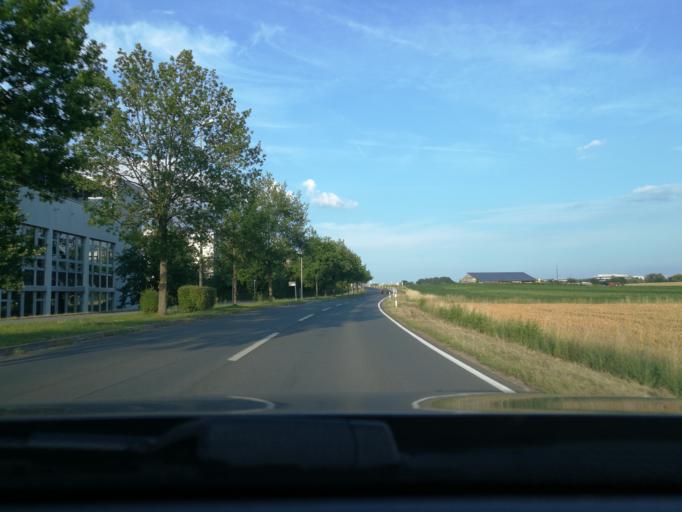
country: DE
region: Bavaria
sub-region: Regierungsbezirk Mittelfranken
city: Erlangen
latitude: 49.5532
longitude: 11.0034
